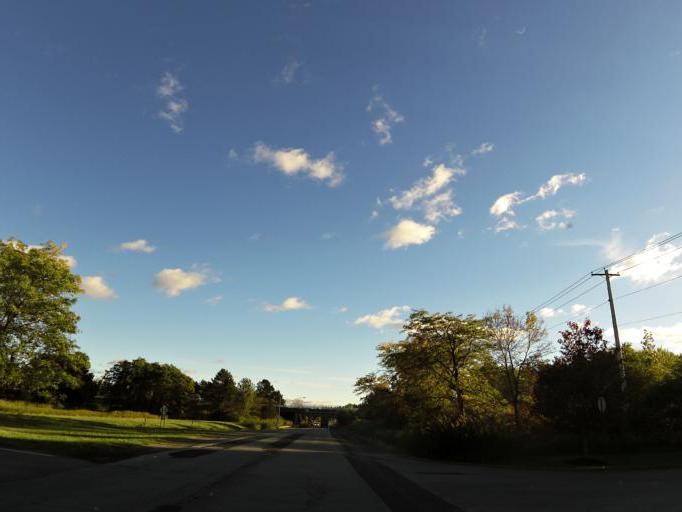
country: US
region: New York
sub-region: Erie County
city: Billington Heights
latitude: 42.7988
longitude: -78.6214
